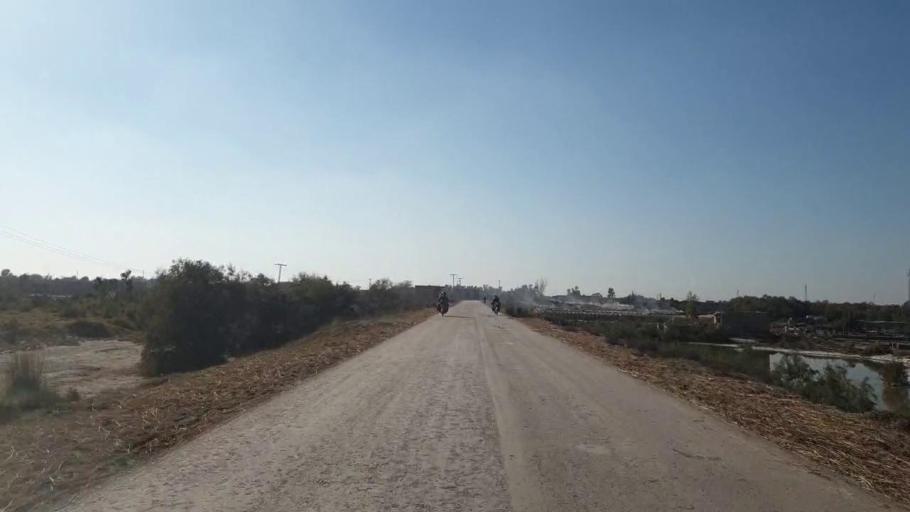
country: PK
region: Sindh
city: New Badah
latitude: 27.3248
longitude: 68.0358
